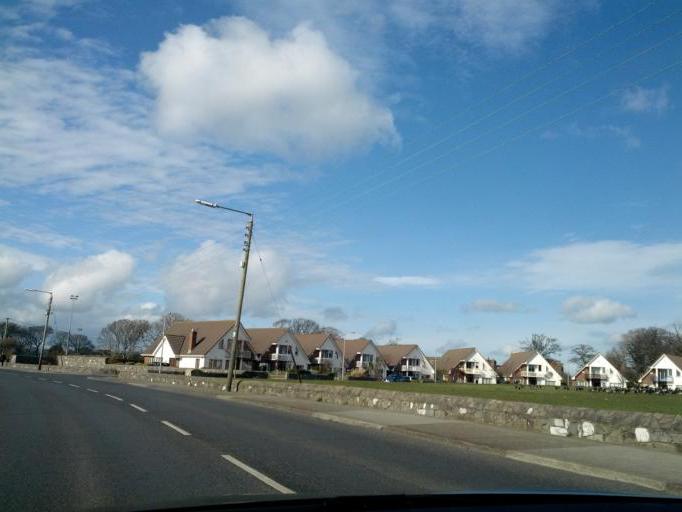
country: IE
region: Leinster
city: Sutton
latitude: 53.3847
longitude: -6.1006
